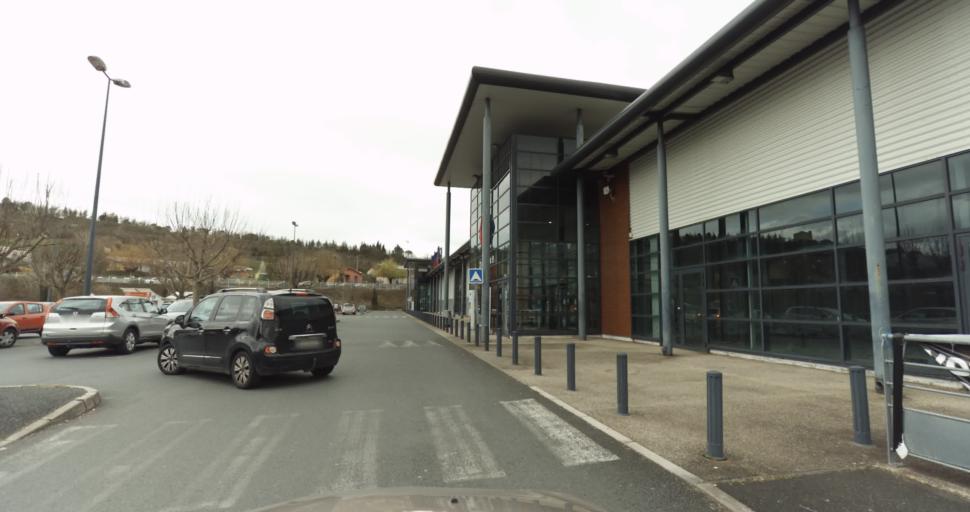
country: FR
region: Midi-Pyrenees
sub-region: Departement du Tarn
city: Puygouzon
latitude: 43.8916
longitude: 2.1664
